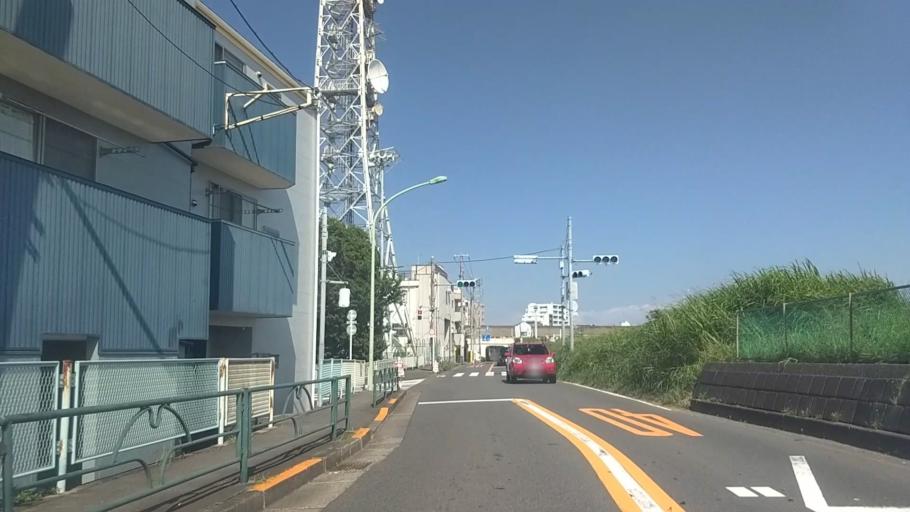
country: JP
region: Kanagawa
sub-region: Kawasaki-shi
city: Kawasaki
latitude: 35.5577
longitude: 139.6942
